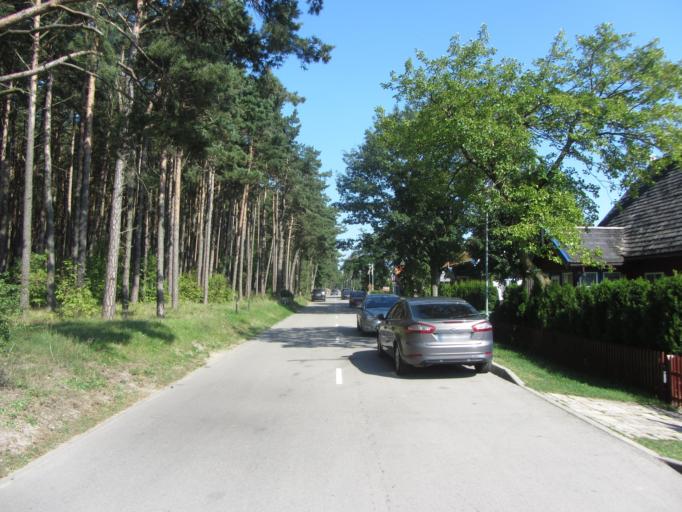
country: LT
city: Neringa
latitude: 55.3679
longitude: 21.0569
